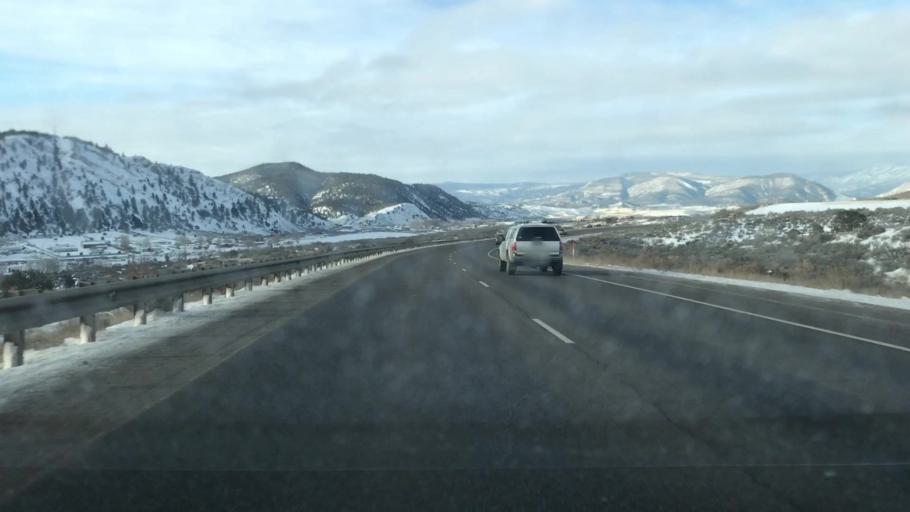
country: US
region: Colorado
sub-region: Eagle County
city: Eagle
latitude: 39.6545
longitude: -106.8527
